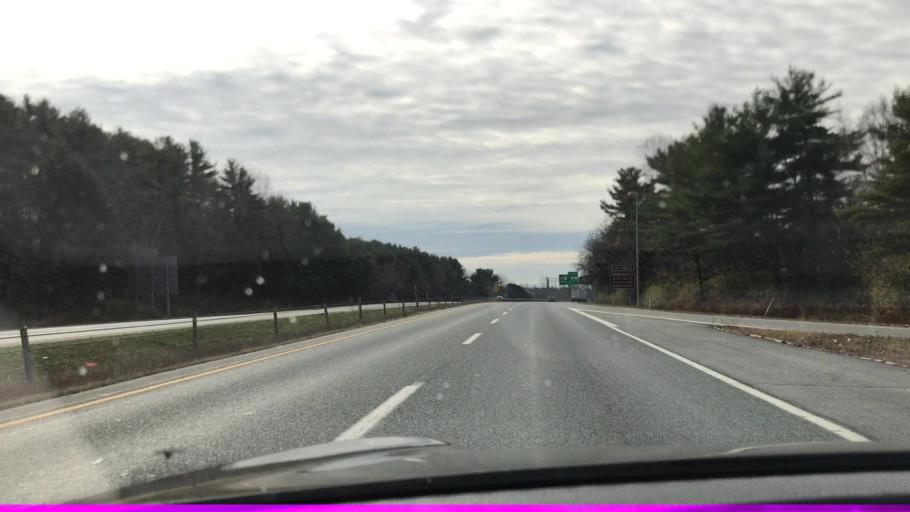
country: US
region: Maine
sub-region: Penobscot County
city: Bangor
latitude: 44.7954
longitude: -68.8032
